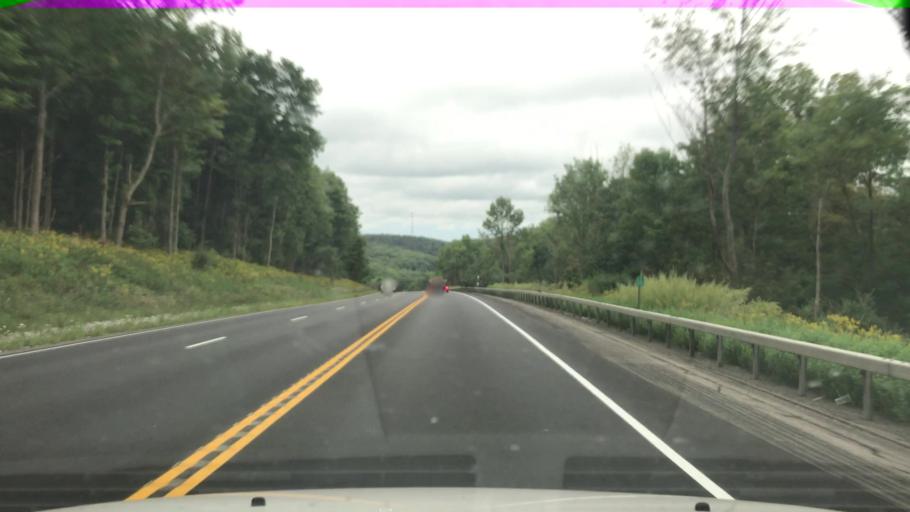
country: US
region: New York
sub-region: Erie County
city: Springville
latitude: 42.3439
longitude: -78.6556
